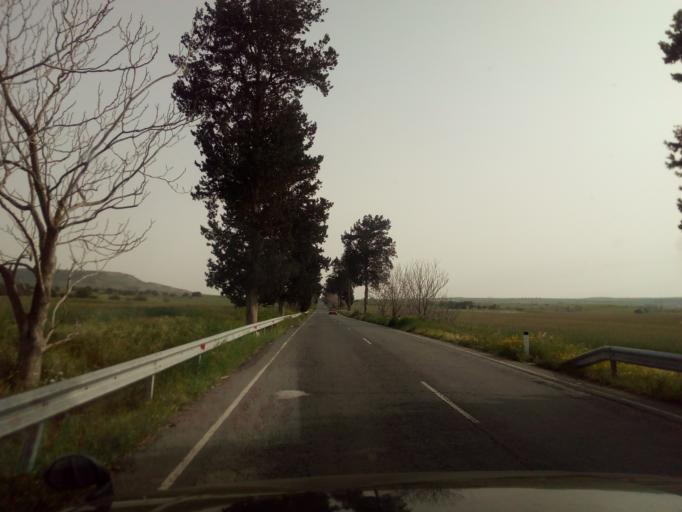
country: CY
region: Lefkosia
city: Lympia
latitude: 35.0276
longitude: 33.4931
